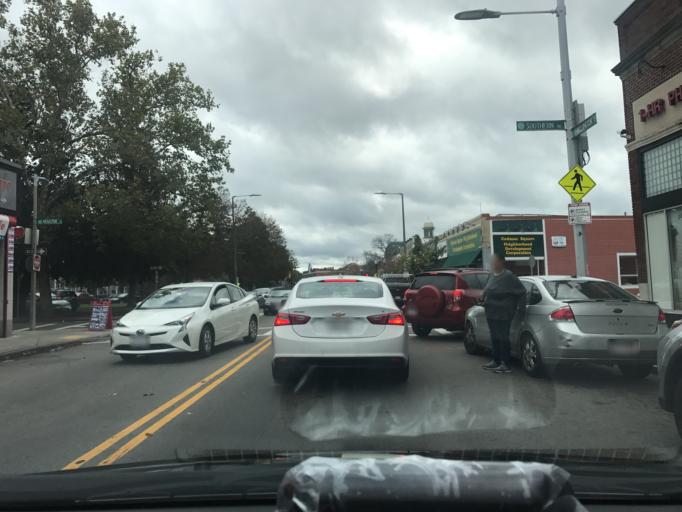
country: US
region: Massachusetts
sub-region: Norfolk County
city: Milton
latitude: 42.2913
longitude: -71.0717
